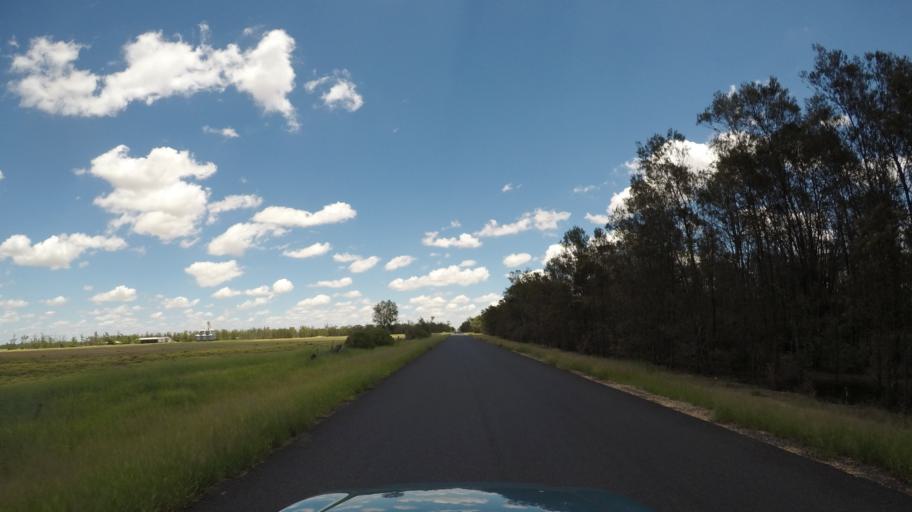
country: AU
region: Queensland
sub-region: Goondiwindi
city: Goondiwindi
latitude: -28.1683
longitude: 150.4553
